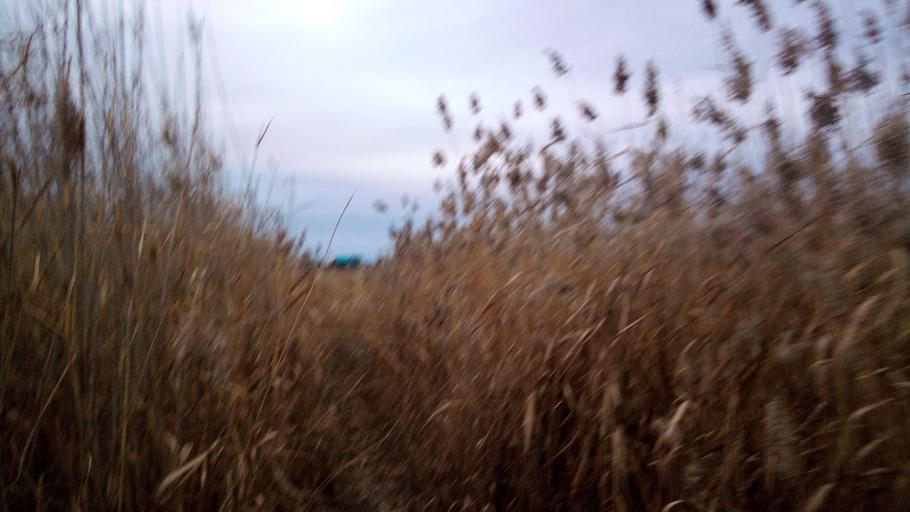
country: RU
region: Chelyabinsk
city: Novosineglazovskiy
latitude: 54.9863
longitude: 61.4032
